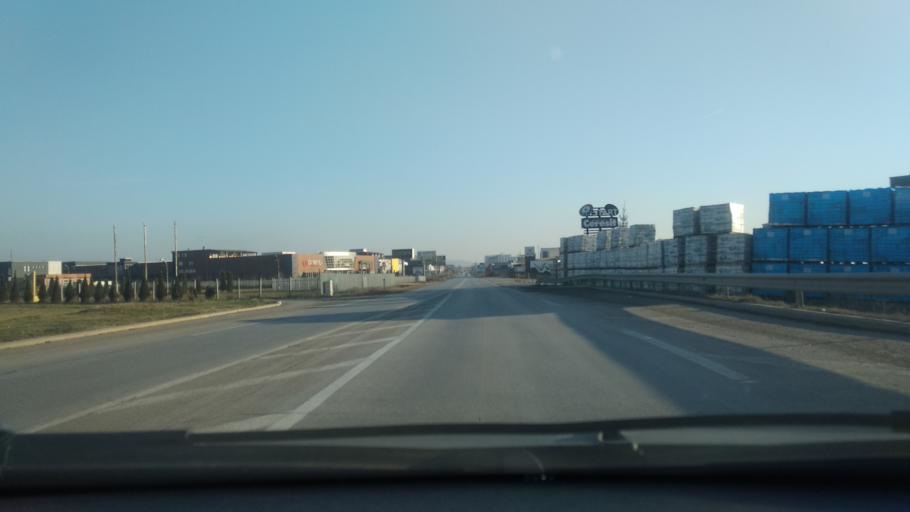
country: XK
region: Pristina
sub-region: Lipjan
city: Lipljan
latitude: 42.5616
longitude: 21.1336
